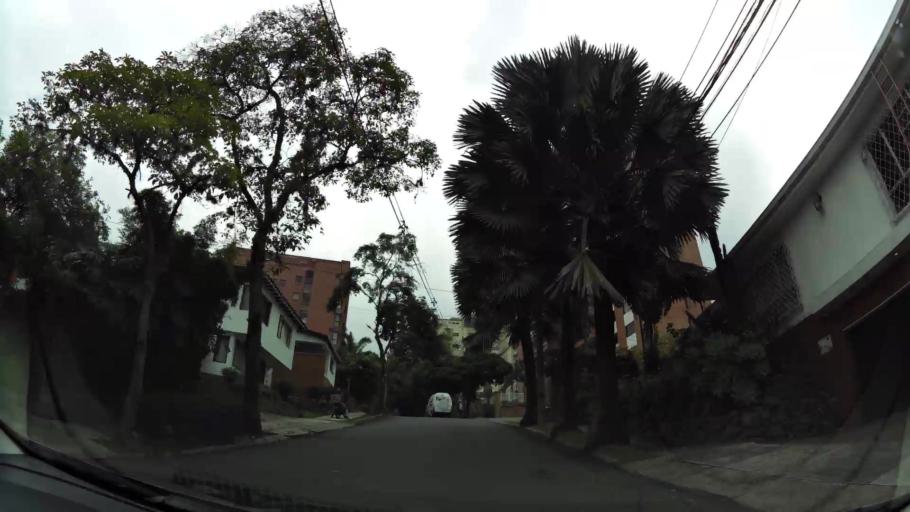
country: CO
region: Antioquia
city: Medellin
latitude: 6.2134
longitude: -75.5623
